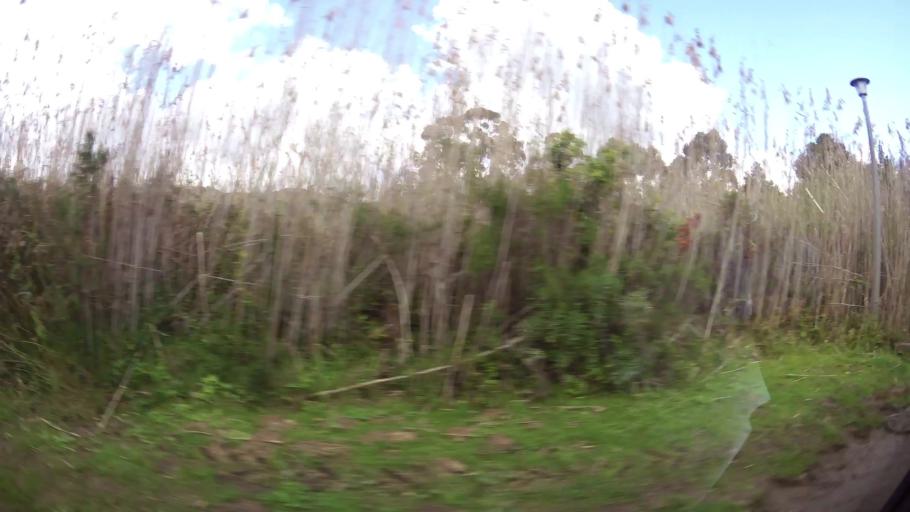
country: ZA
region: Western Cape
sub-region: Eden District Municipality
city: Knysna
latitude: -34.0576
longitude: 23.0798
